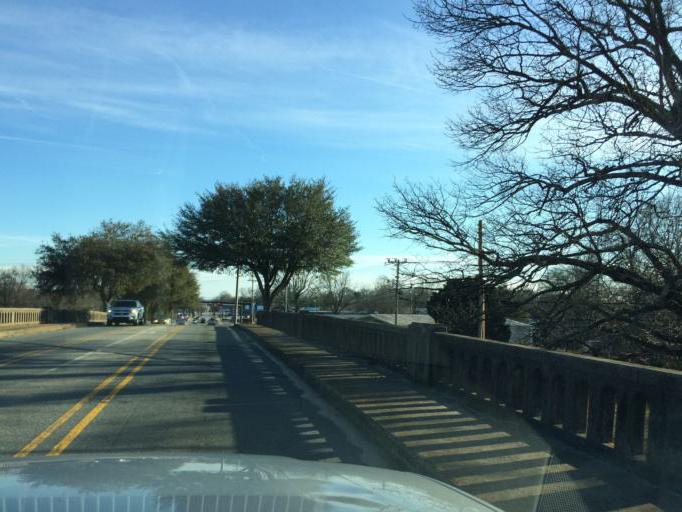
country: US
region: North Carolina
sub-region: Rutherford County
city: Forest City
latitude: 35.3293
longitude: -81.8629
